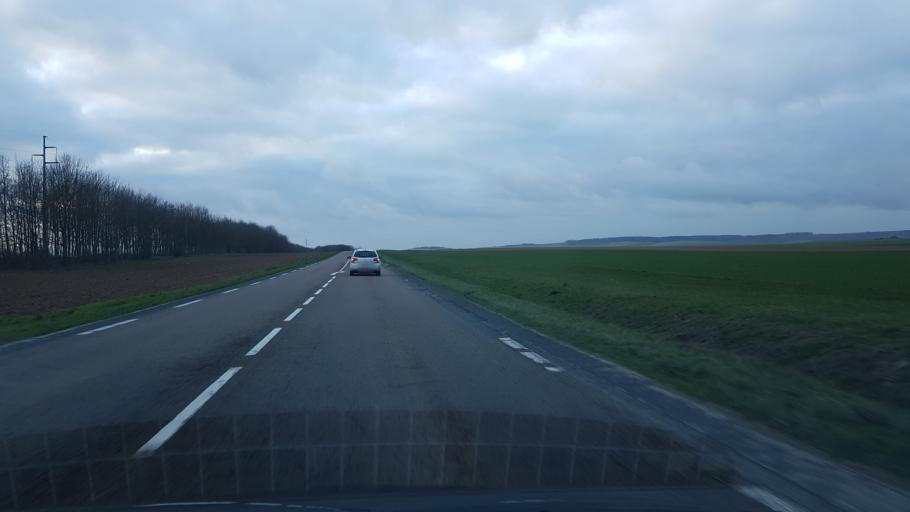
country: FR
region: Champagne-Ardenne
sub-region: Departement de la Marne
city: Connantre
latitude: 48.7245
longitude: 3.8251
